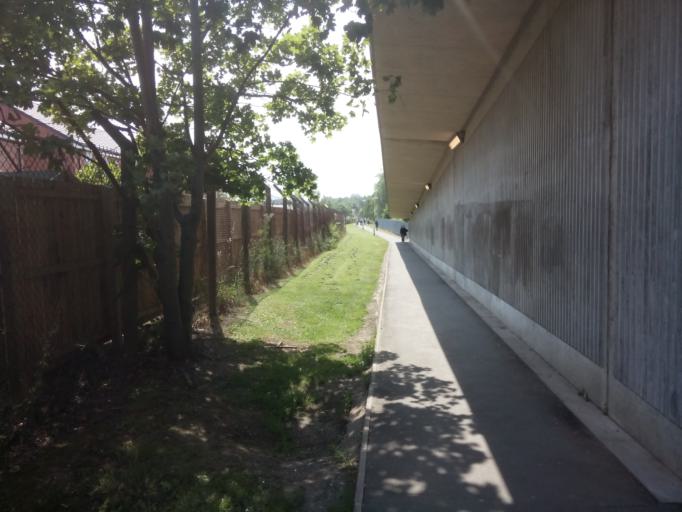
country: GB
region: England
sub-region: Northumberland
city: Backworth
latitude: 55.0238
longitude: -1.5408
